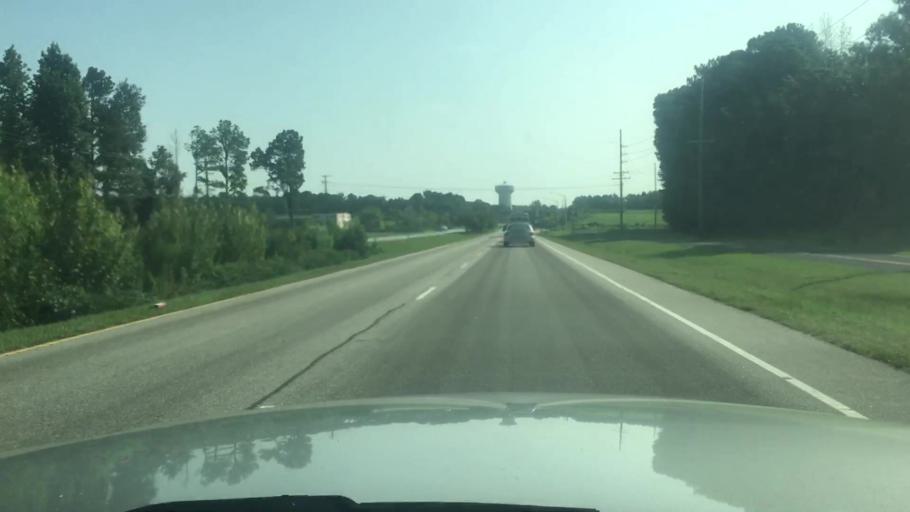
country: US
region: North Carolina
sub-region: Cumberland County
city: Fayetteville
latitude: 35.0304
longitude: -78.8807
